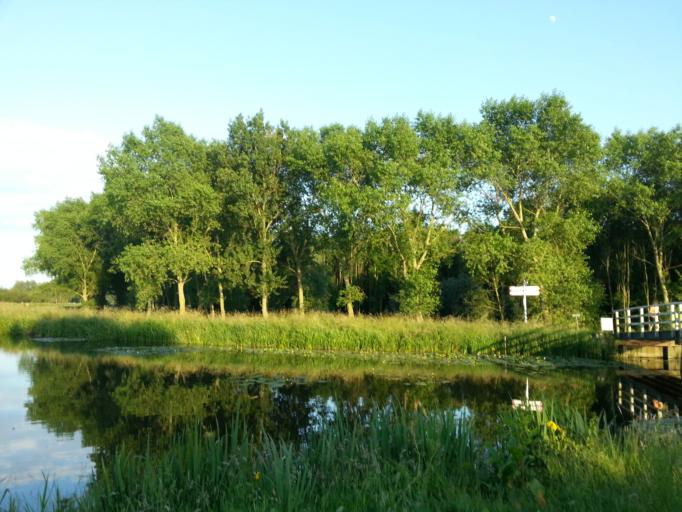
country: NL
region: South Holland
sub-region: Gemeente Den Haag
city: Ypenburg
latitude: 52.0330
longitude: 4.3939
